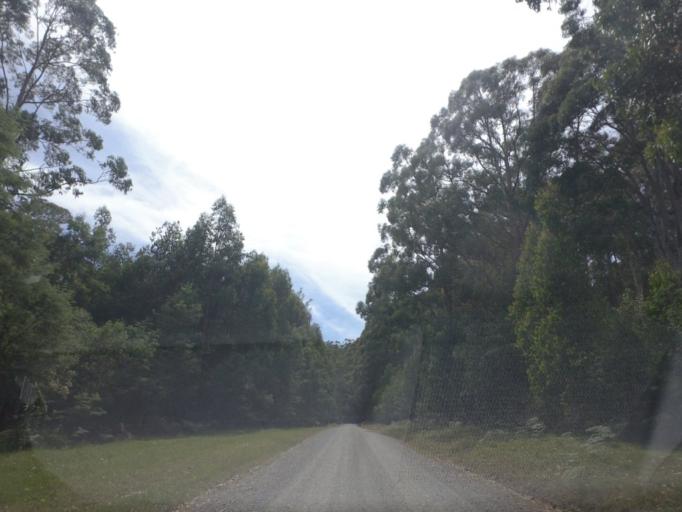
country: AU
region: Victoria
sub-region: Yarra Ranges
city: Healesville
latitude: -37.5557
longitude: 145.5101
